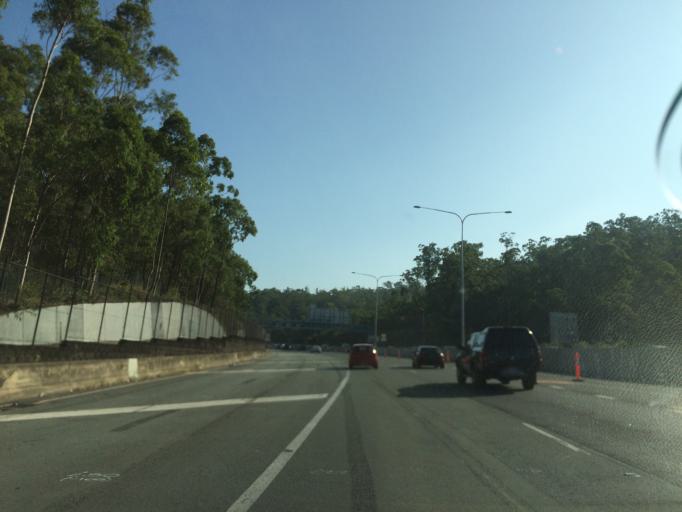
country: AU
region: Queensland
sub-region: Brisbane
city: Taringa
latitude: -27.4827
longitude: 152.9696
